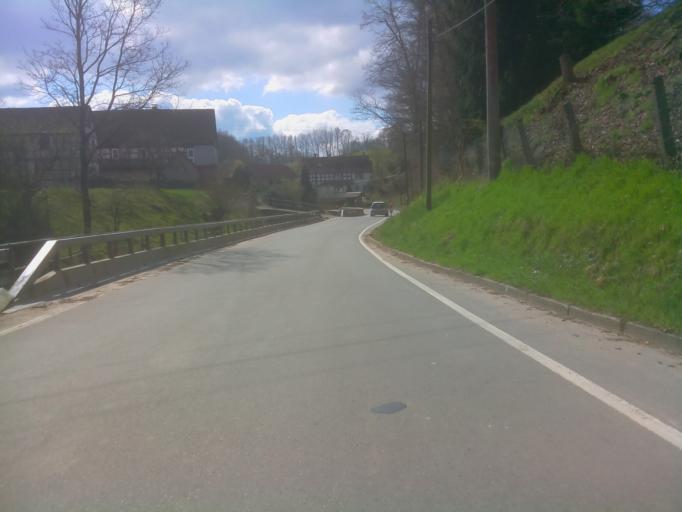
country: DE
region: Thuringia
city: Karlsdorf
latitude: 50.7981
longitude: 11.7979
